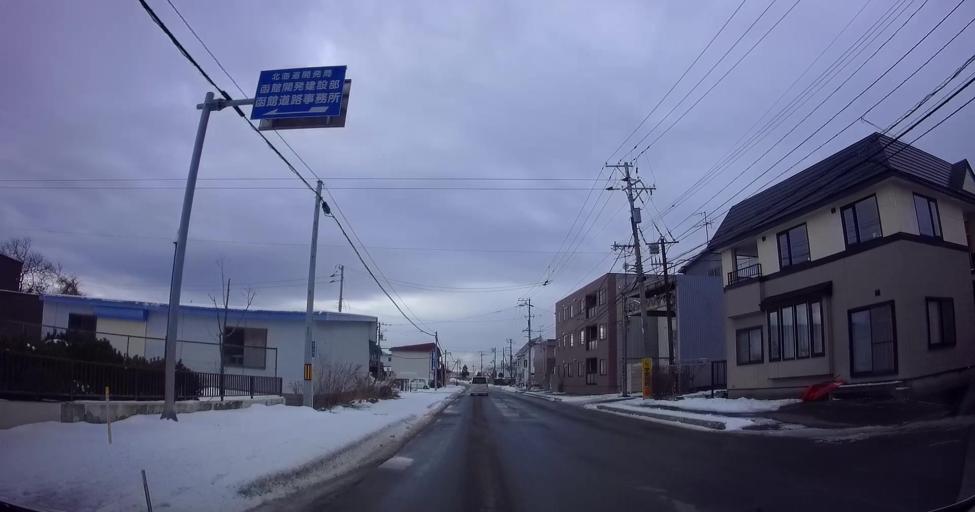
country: JP
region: Hokkaido
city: Kamiiso
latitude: 41.8280
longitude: 140.6865
